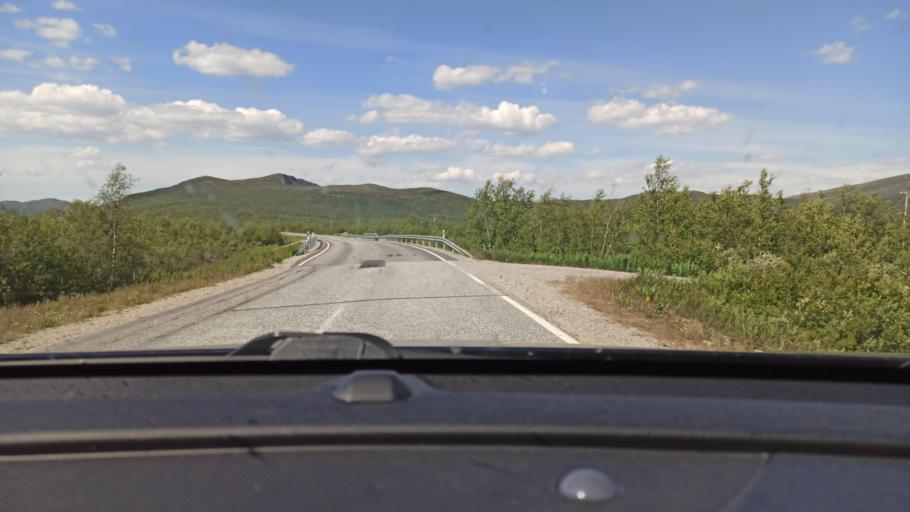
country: NO
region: Troms
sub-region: Nordreisa
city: Storslett
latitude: 68.8802
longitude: 21.0793
